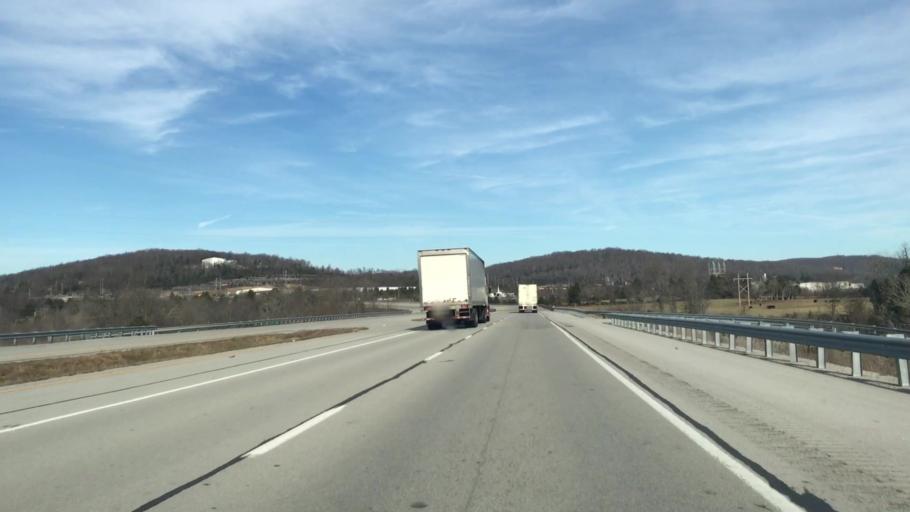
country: US
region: Kentucky
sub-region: Pulaski County
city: Somerset
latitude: 37.0414
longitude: -84.5862
